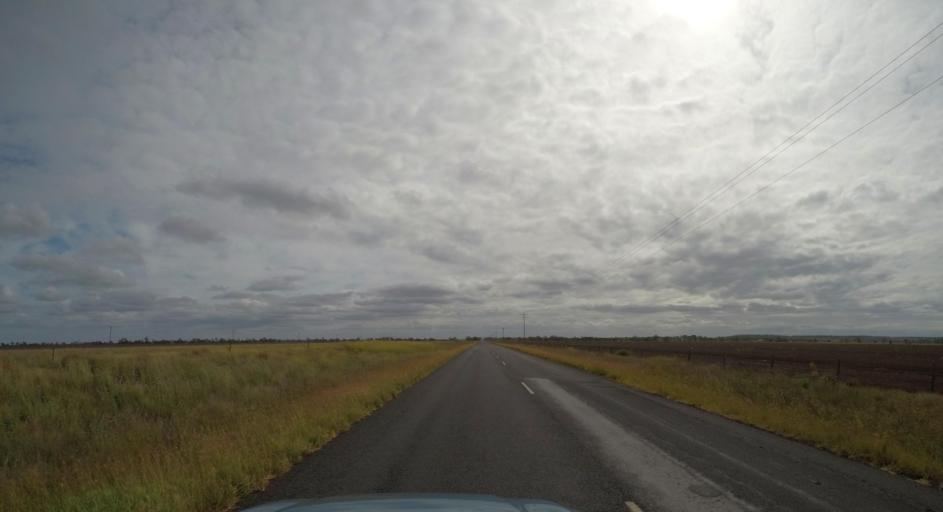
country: AU
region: Queensland
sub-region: Western Downs
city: Dalby
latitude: -26.9950
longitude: 151.2306
